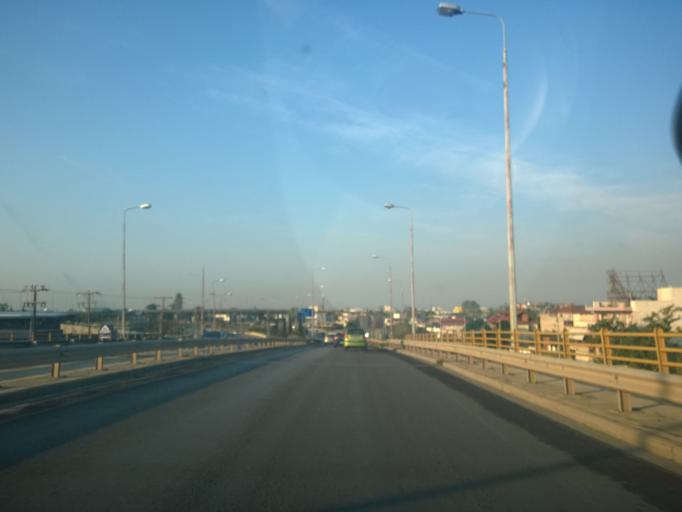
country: GR
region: Central Macedonia
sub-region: Nomos Thessalonikis
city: Menemeni
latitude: 40.6563
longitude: 22.9026
